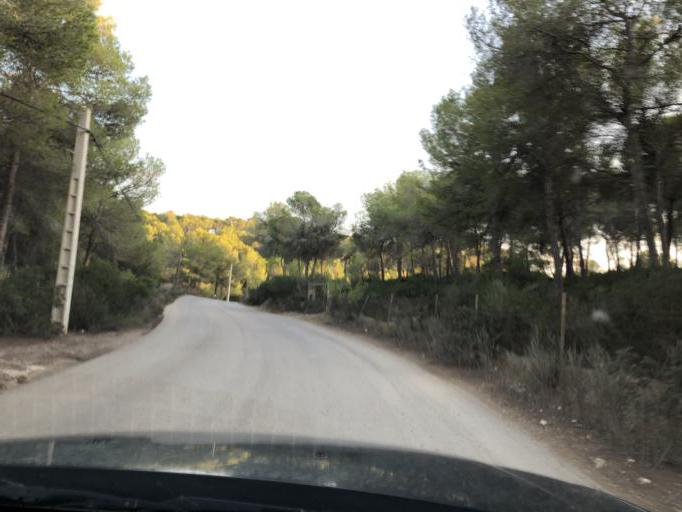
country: ES
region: Balearic Islands
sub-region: Illes Balears
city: Santa Ponsa
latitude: 39.5310
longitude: 2.4810
